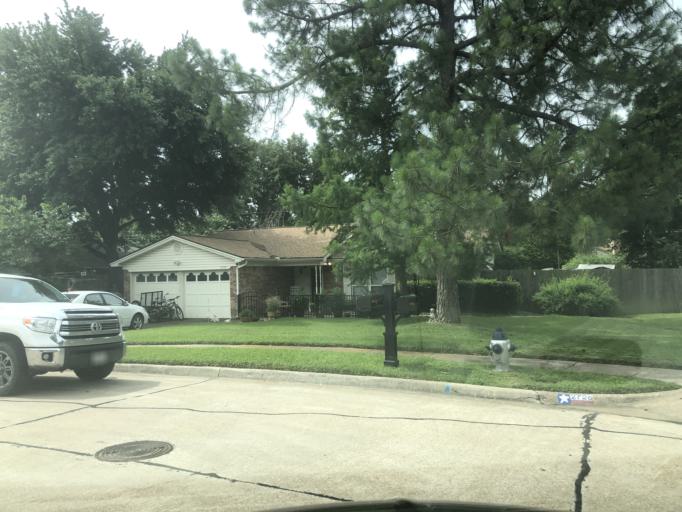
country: US
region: Texas
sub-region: Dallas County
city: Irving
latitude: 32.7959
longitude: -96.9835
